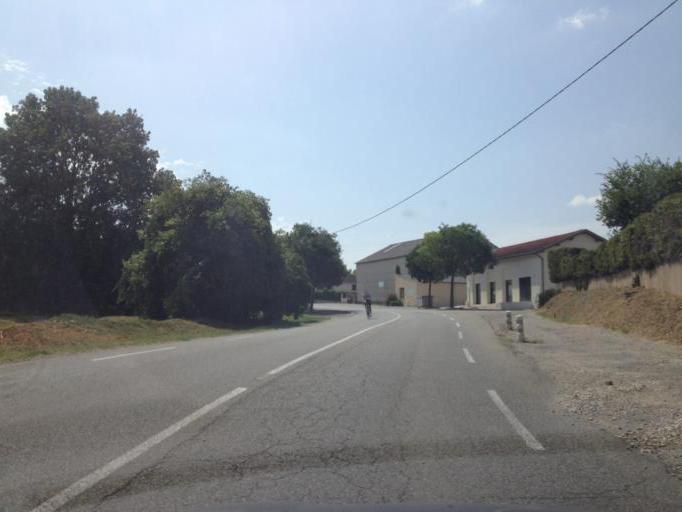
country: FR
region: Rhone-Alpes
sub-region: Departement de la Drome
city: Chatuzange-le-Goubet
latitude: 45.0099
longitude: 5.0889
